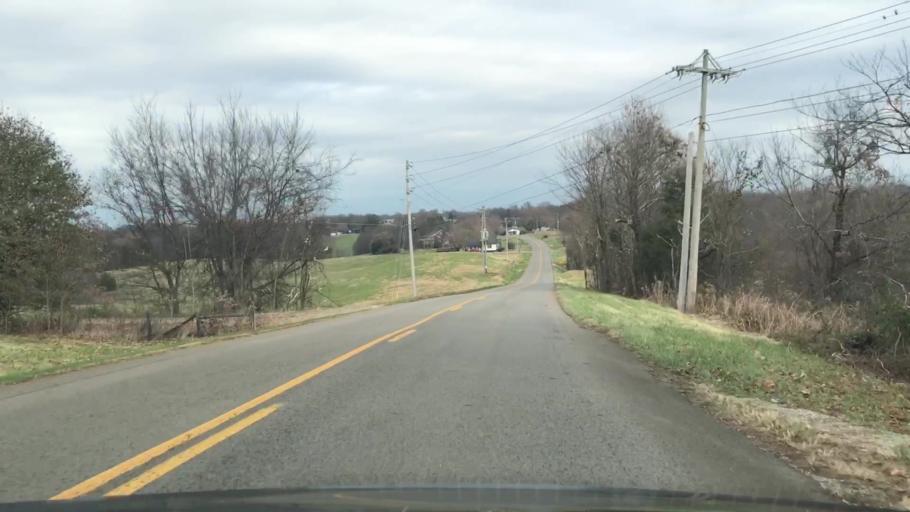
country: US
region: Kentucky
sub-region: Metcalfe County
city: Edmonton
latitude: 36.8848
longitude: -85.6660
